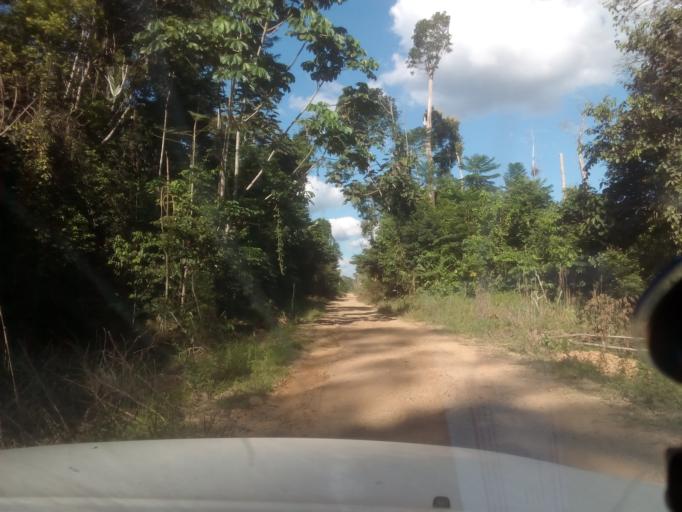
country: PE
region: Cusco
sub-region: Provincia de Quispicanchis
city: Quince Mil
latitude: -12.6433
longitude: -70.3654
